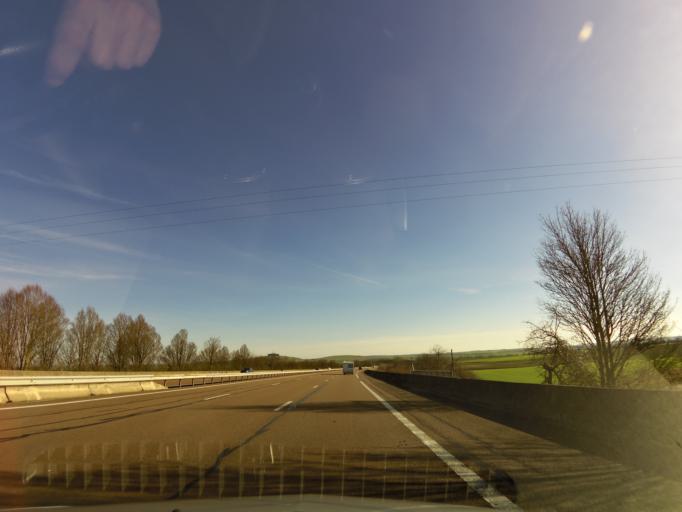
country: FR
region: Bourgogne
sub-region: Departement de l'Yonne
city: Aillant-sur-Tholon
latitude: 47.9102
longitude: 3.3328
